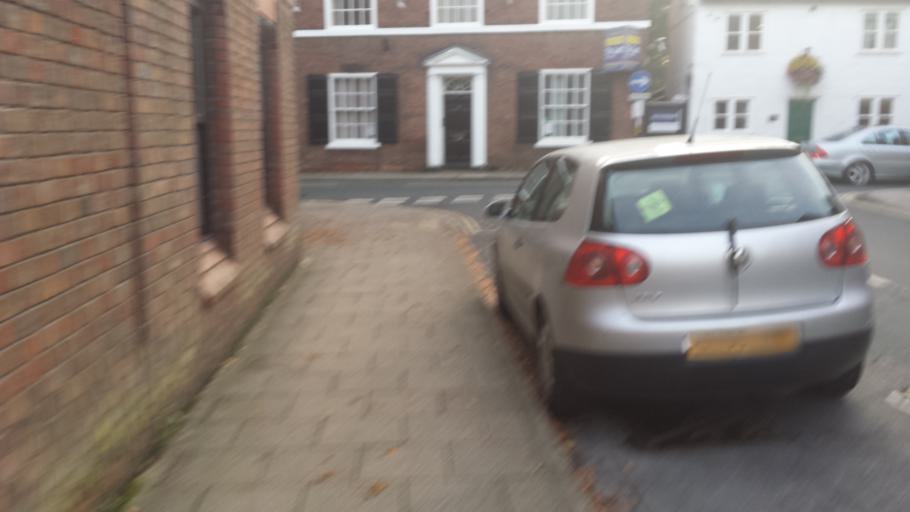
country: GB
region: England
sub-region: East Riding of Yorkshire
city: Beverley
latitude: 53.8413
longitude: -0.4315
